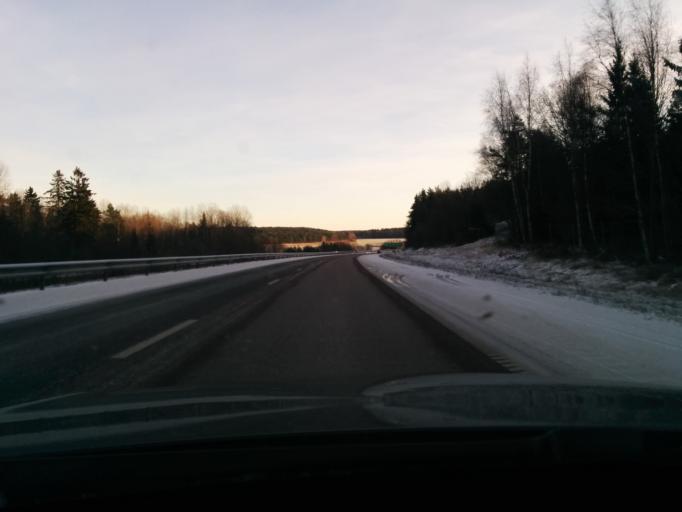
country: SE
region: Uppsala
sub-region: Habo Kommun
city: Balsta
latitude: 59.5918
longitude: 17.4894
